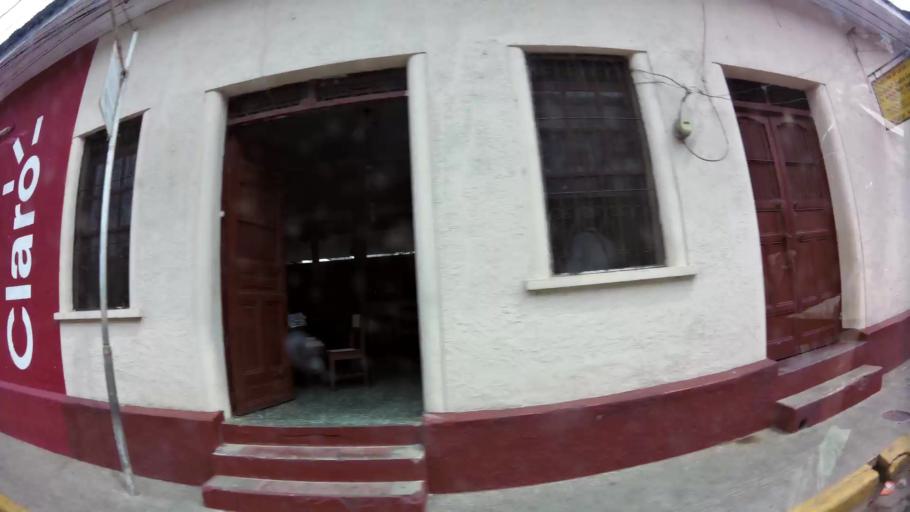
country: NI
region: Rivas
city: Rivas
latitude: 11.4400
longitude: -85.8293
